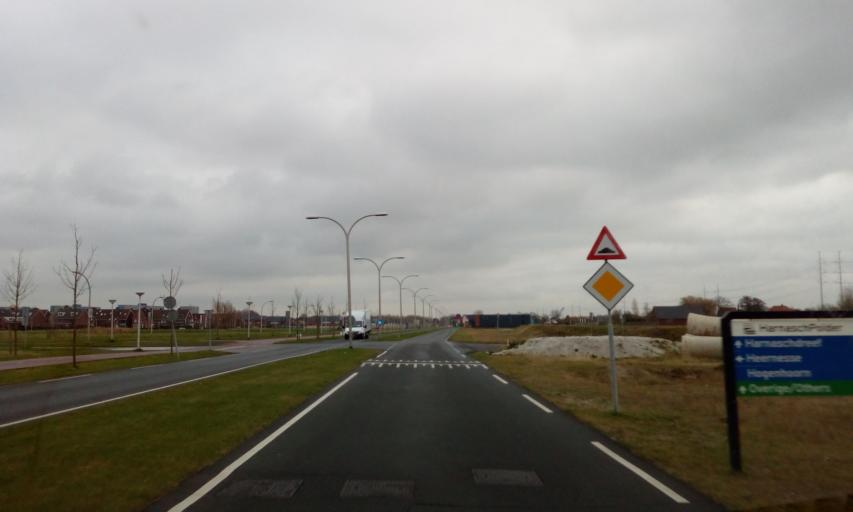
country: NL
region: South Holland
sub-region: Gemeente Rijswijk
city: Rijswijk
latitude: 52.0028
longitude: 4.3177
